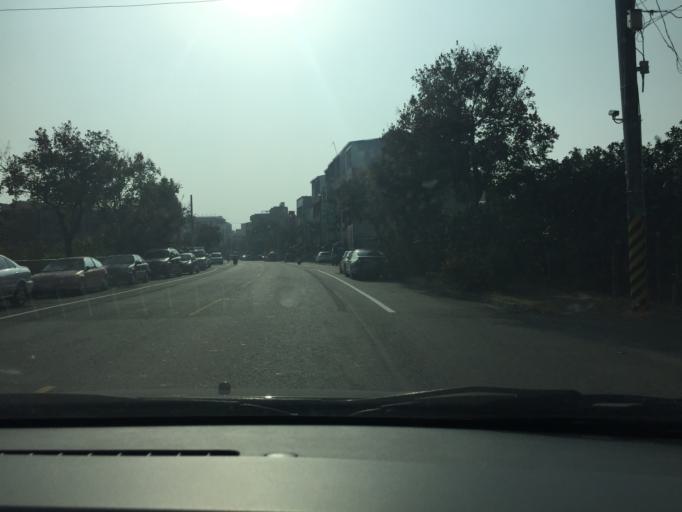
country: TW
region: Taiwan
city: Xinying
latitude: 23.1849
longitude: 120.2572
